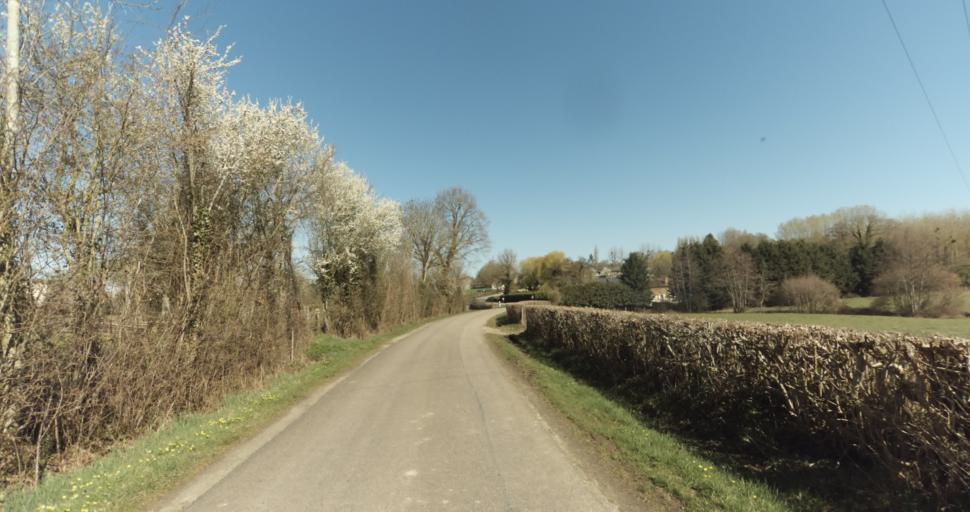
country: FR
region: Lower Normandy
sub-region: Departement du Calvados
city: Livarot
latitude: 49.0114
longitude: 0.0743
